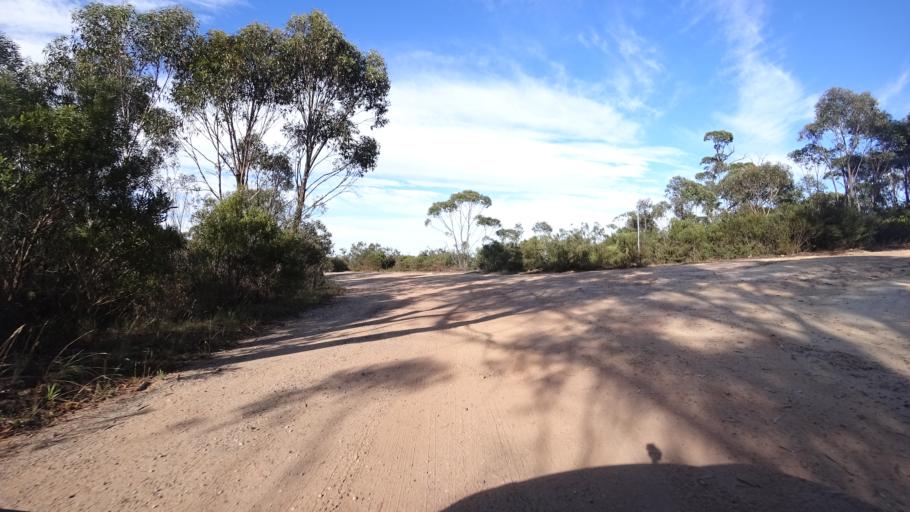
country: AU
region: New South Wales
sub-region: Lithgow
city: Lithgow
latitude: -33.5133
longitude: 150.1511
